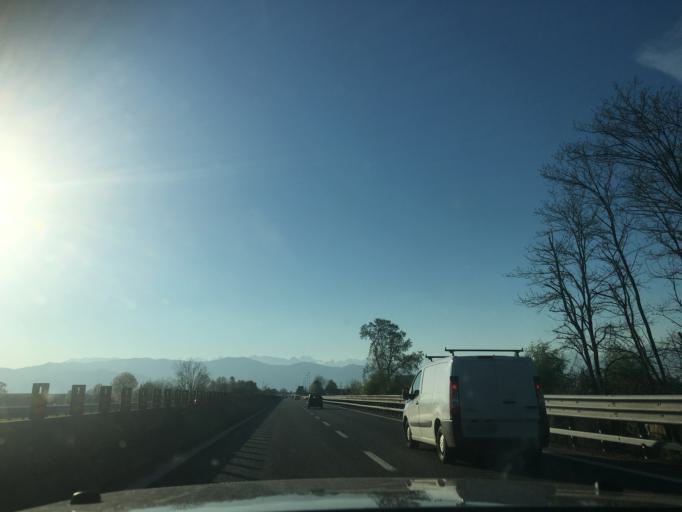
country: IT
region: Piedmont
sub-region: Provincia di Torino
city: Caselle Torinese
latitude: 45.1761
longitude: 7.6639
